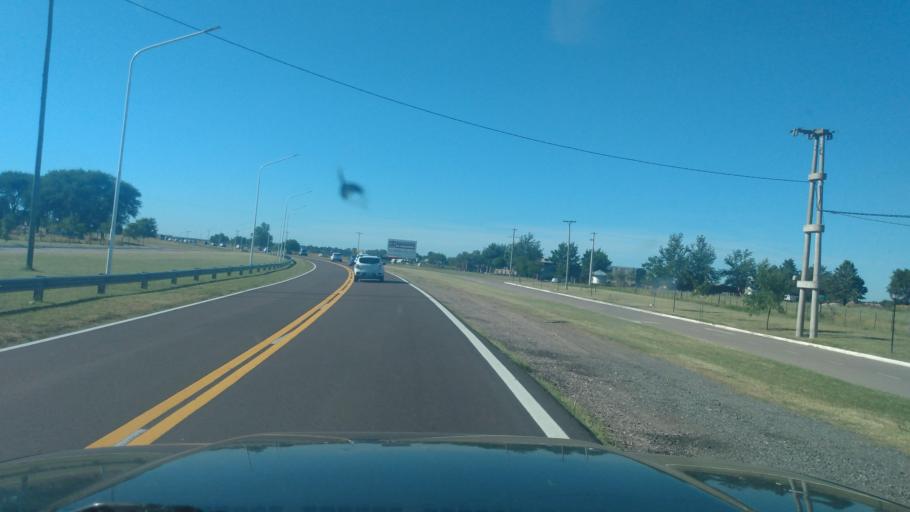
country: AR
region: La Pampa
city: Doblas
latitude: -37.0345
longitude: -64.2889
